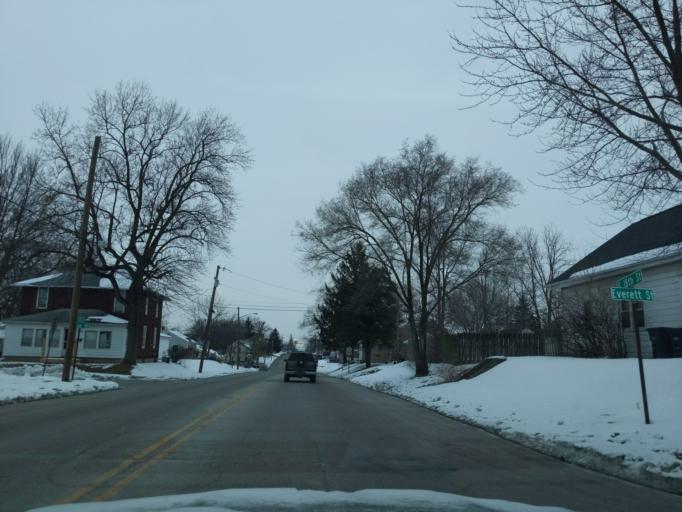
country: US
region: Indiana
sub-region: Tippecanoe County
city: Lafayette
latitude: 40.4133
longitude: -86.8771
